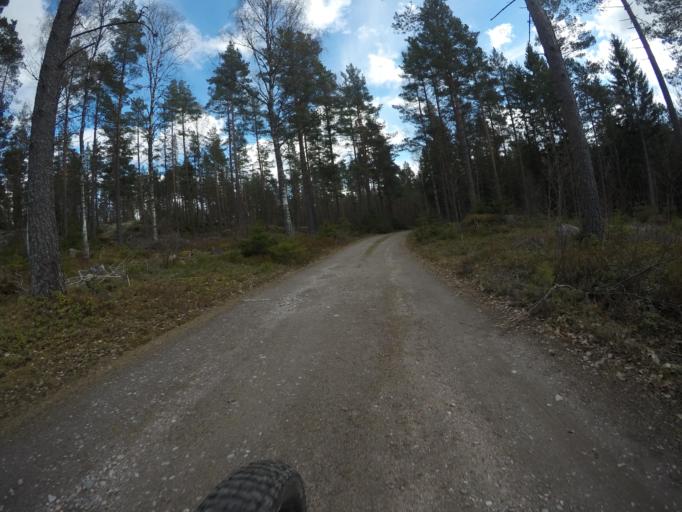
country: SE
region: Vaestmanland
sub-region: Kungsors Kommun
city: Kungsoer
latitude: 59.3658
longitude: 16.1035
